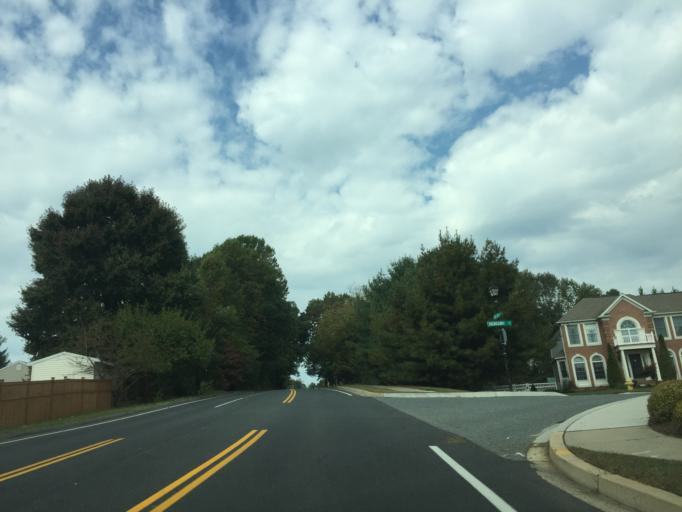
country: US
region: Maryland
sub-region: Harford County
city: Bel Air South
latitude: 39.4874
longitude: -76.3049
